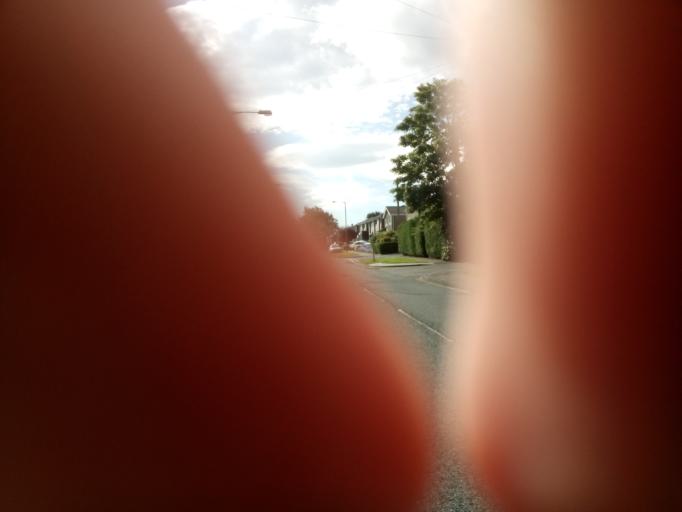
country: GB
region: England
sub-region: County Durham
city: Durham
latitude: 54.8036
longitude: -1.5665
